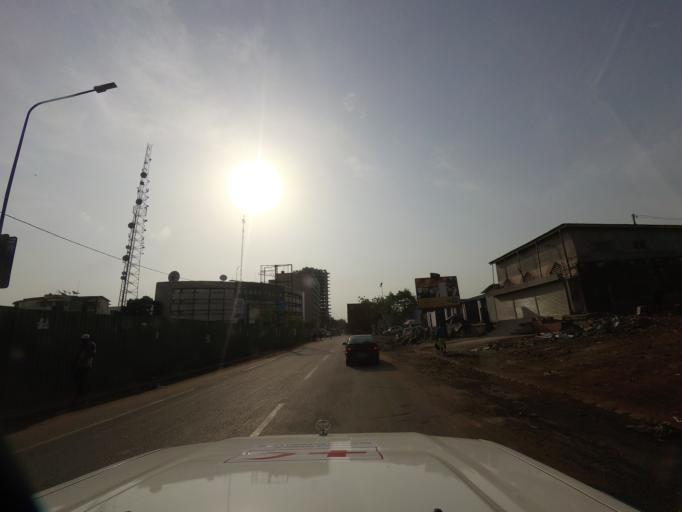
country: GN
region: Conakry
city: Camayenne
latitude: 9.5146
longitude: -13.7116
